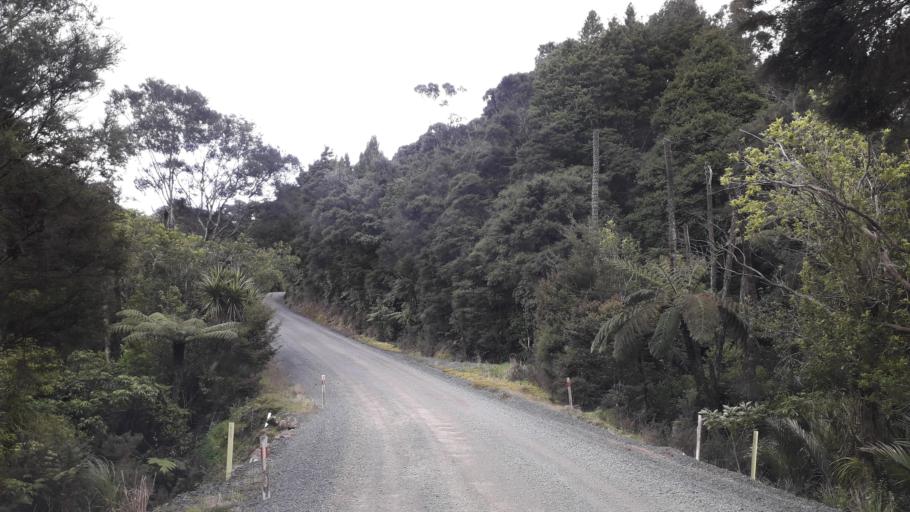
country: NZ
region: Northland
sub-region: Far North District
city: Paihia
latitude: -35.3205
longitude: 174.2336
